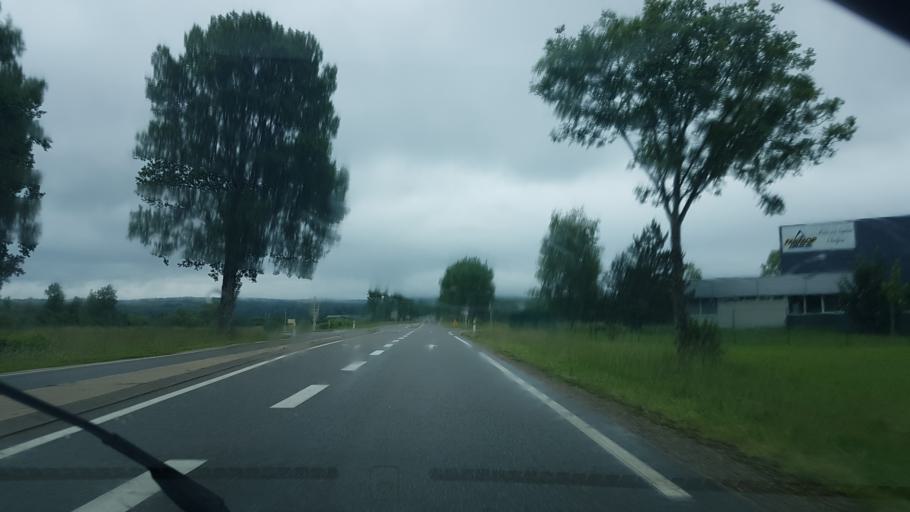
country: FR
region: Franche-Comte
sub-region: Departement du Jura
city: Clairvaux-les-Lacs
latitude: 46.5894
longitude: 5.7183
